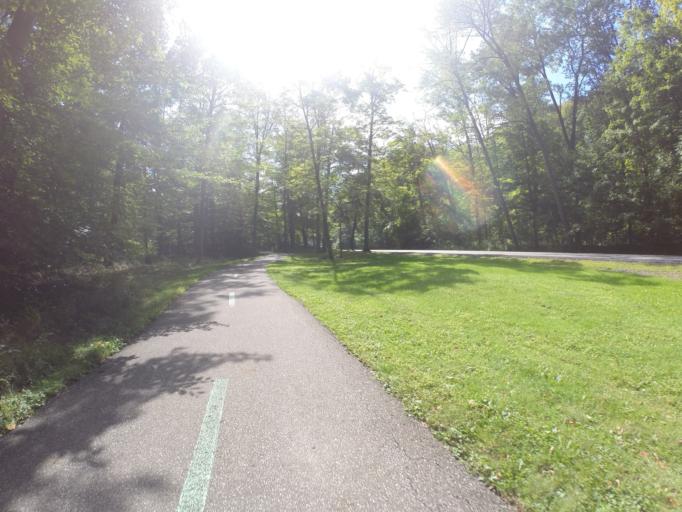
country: US
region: Ohio
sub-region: Cuyahoga County
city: Richmond Heights
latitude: 41.5462
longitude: -81.5278
